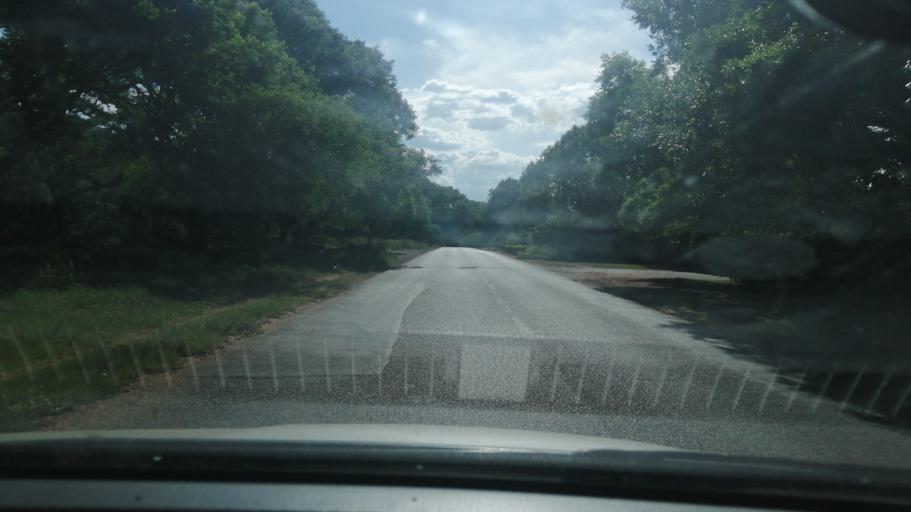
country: ZW
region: Harare
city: Harare
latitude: -17.7952
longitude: 31.0546
